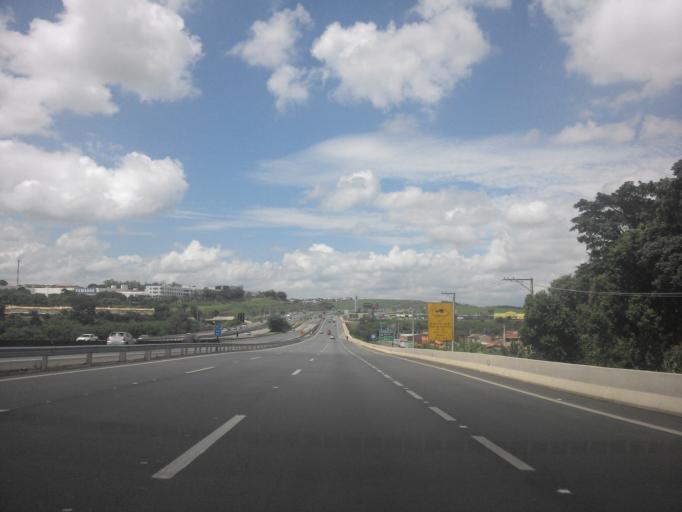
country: BR
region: Sao Paulo
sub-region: Campinas
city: Campinas
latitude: -22.8467
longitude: -47.0335
